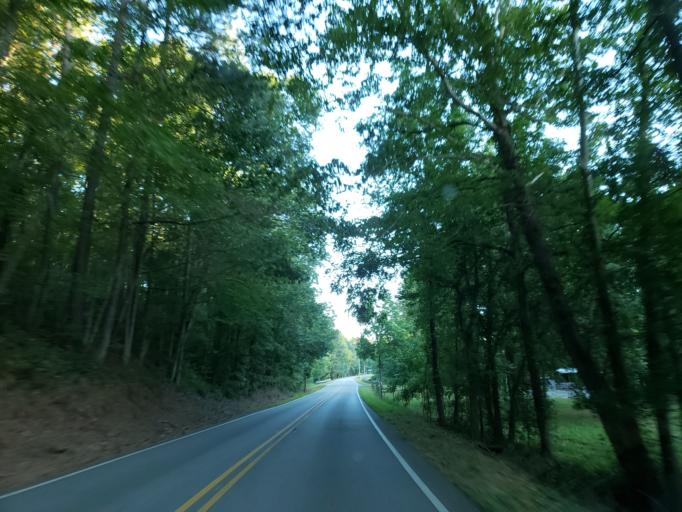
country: US
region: Georgia
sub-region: Bartow County
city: Rydal
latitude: 34.3872
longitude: -84.5921
